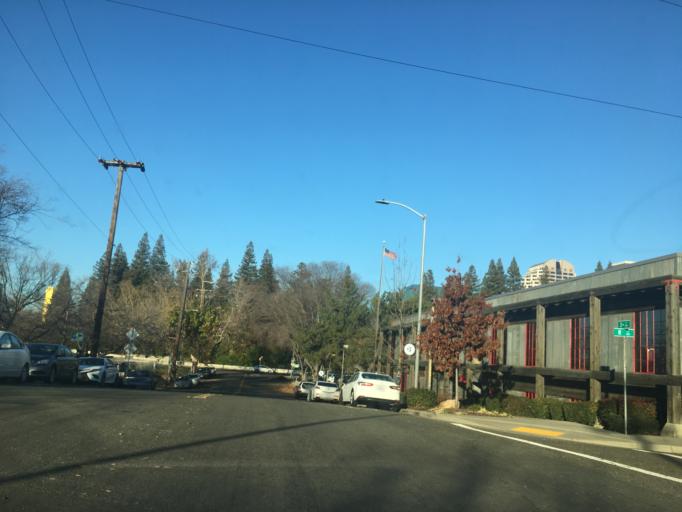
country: US
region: California
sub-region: Sacramento County
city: Sacramento
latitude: 38.5743
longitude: -121.5080
